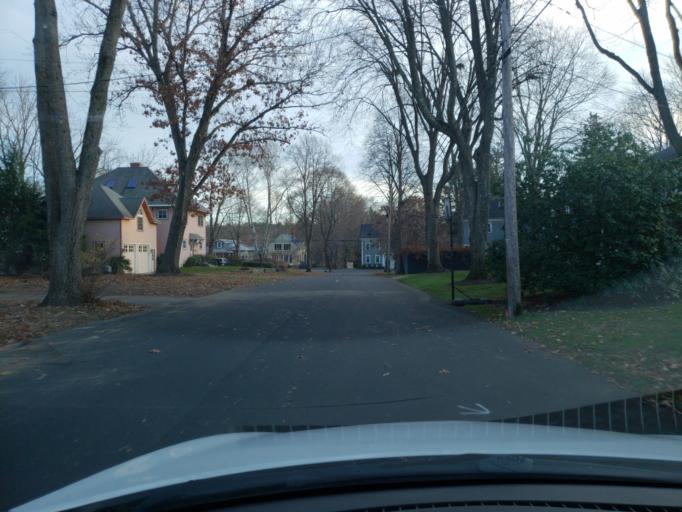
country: US
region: Massachusetts
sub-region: Essex County
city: Andover
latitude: 42.6596
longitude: -71.1346
